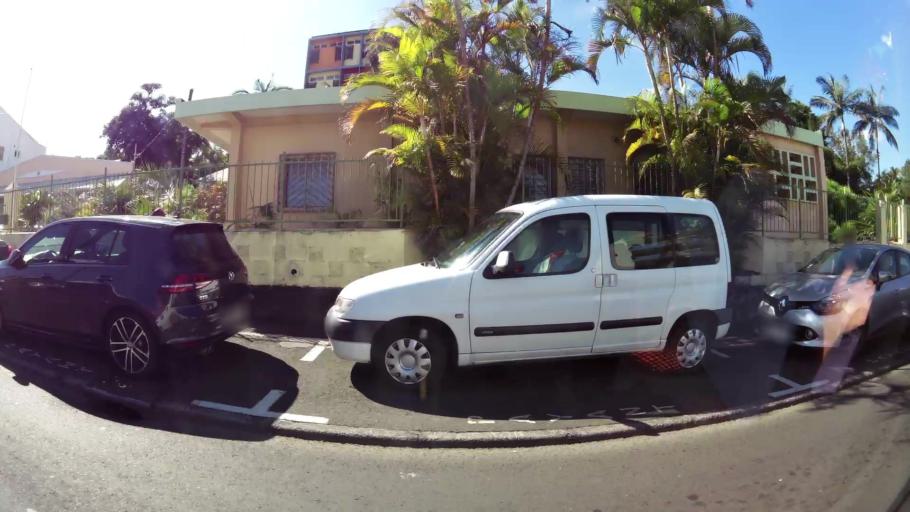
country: RE
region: Reunion
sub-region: Reunion
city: Le Tampon
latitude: -21.2779
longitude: 55.5145
